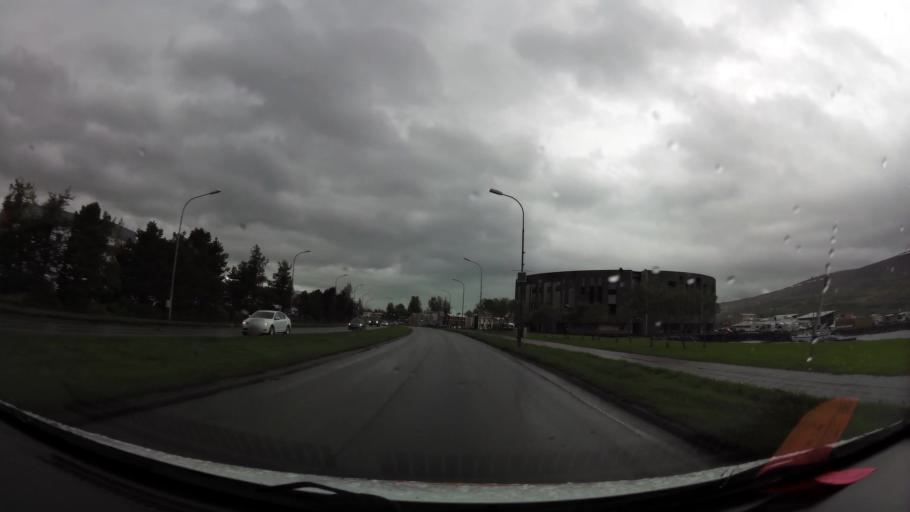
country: IS
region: Northeast
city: Akureyri
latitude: 65.6822
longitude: -18.0874
